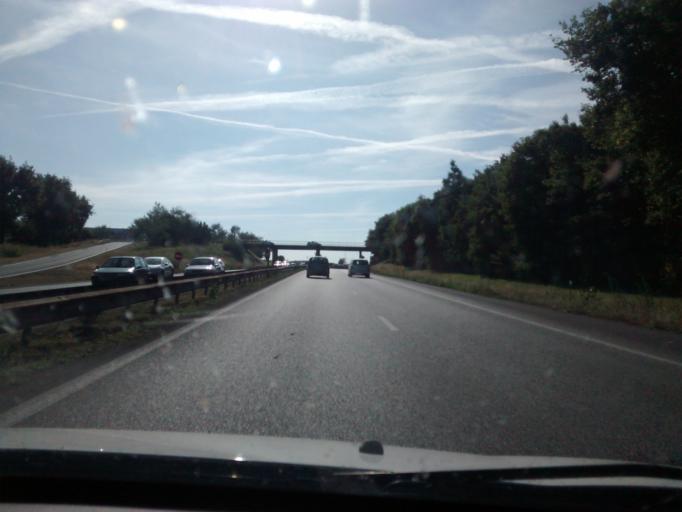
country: FR
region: Brittany
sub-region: Departement d'Ille-et-Vilaine
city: Noyal-sur-Vilaine
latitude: 48.1077
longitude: -1.5190
